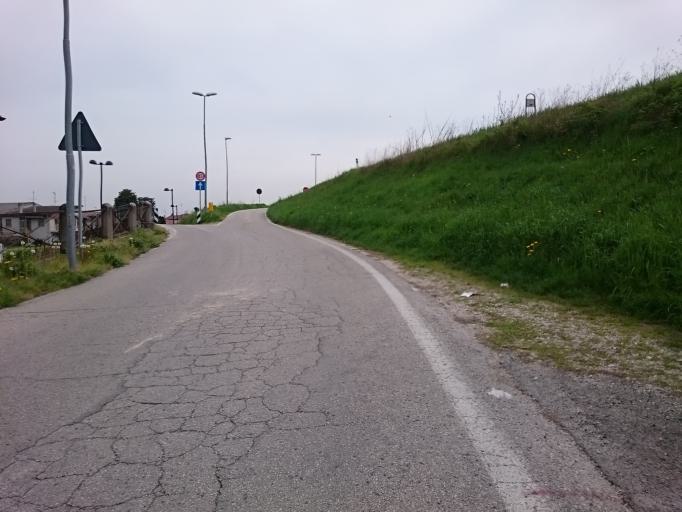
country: IT
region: Veneto
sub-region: Provincia di Padova
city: Anguillara Veneta
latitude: 45.1379
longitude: 11.8856
